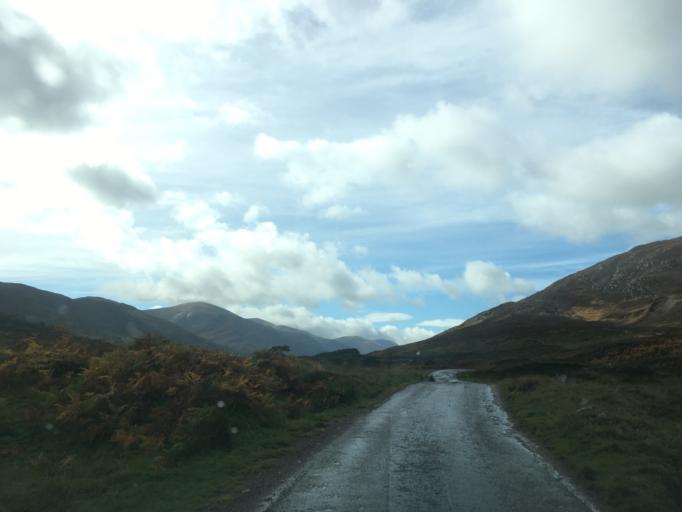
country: GB
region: Scotland
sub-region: Highland
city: Beauly
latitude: 57.3546
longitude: -4.8935
